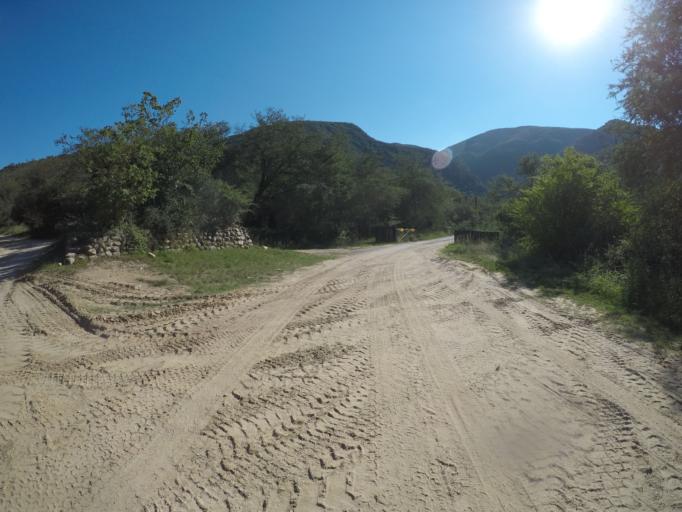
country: ZA
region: Eastern Cape
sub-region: Cacadu District Municipality
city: Kareedouw
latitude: -33.6625
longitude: 24.5404
